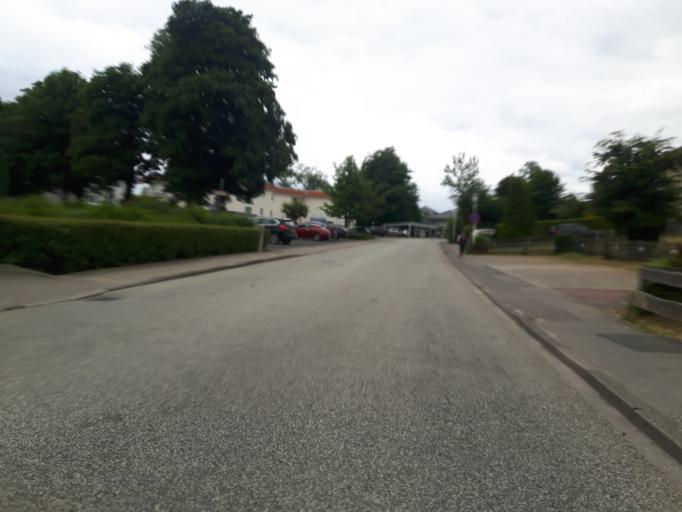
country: DE
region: Schleswig-Holstein
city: Gromitz
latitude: 54.1415
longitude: 10.9506
